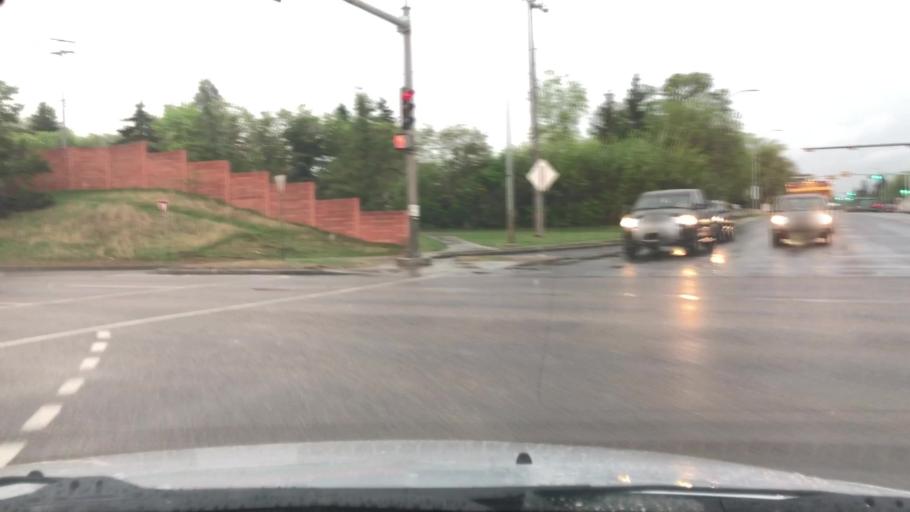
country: CA
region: Alberta
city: Edmonton
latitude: 53.5806
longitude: -113.5412
